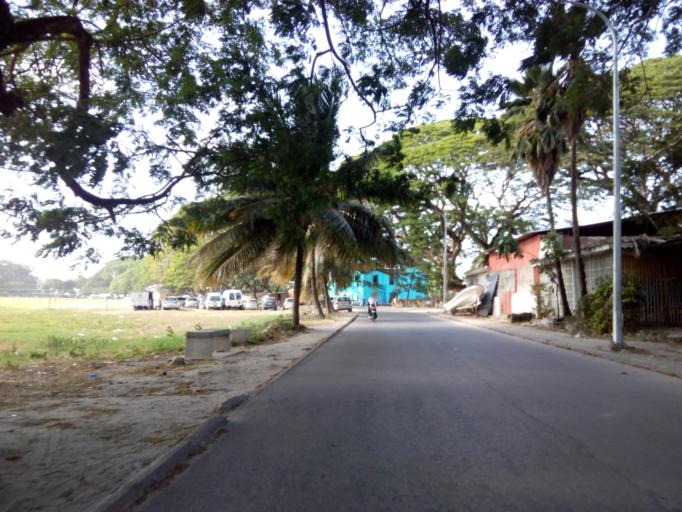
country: TZ
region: Zanzibar Urban/West
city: Zanzibar
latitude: -6.1697
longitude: 39.1944
